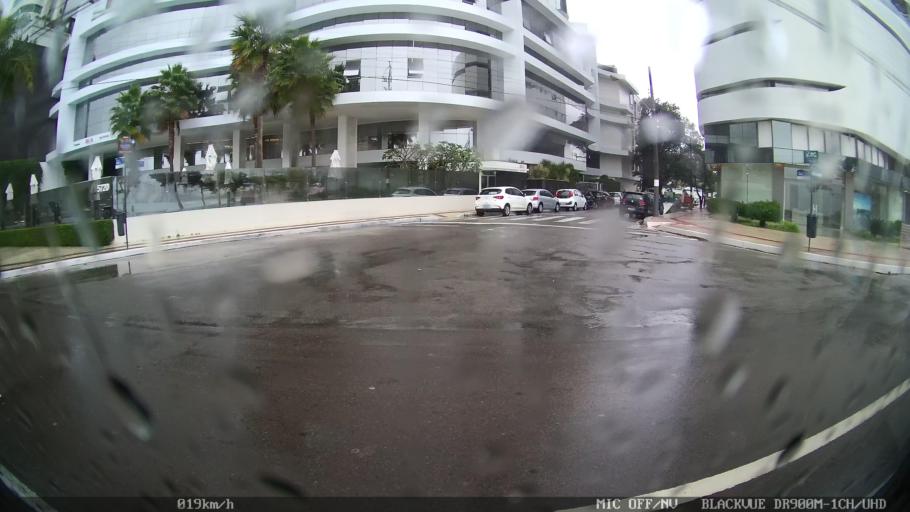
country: BR
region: Santa Catarina
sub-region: Balneario Camboriu
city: Balneario Camboriu
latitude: -27.0056
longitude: -48.6049
